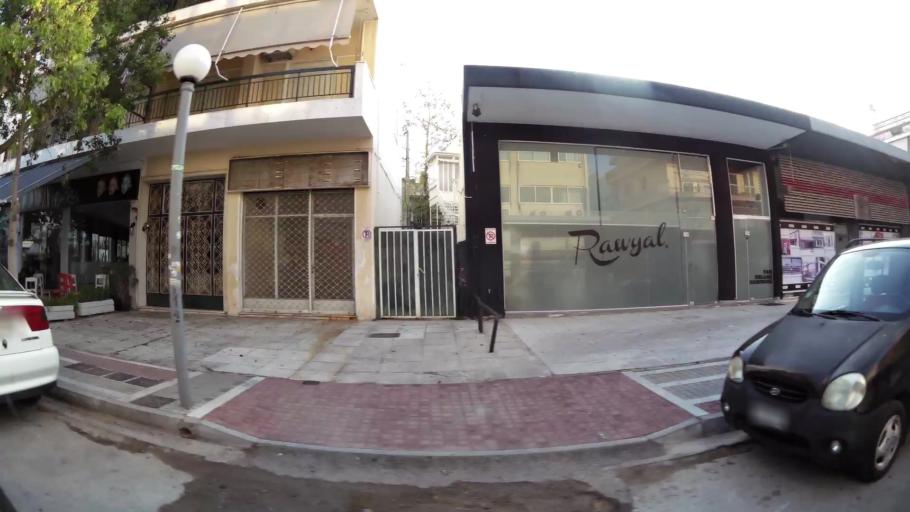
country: GR
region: Attica
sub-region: Nomarchia Athinas
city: Ymittos
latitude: 37.9439
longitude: 23.7436
